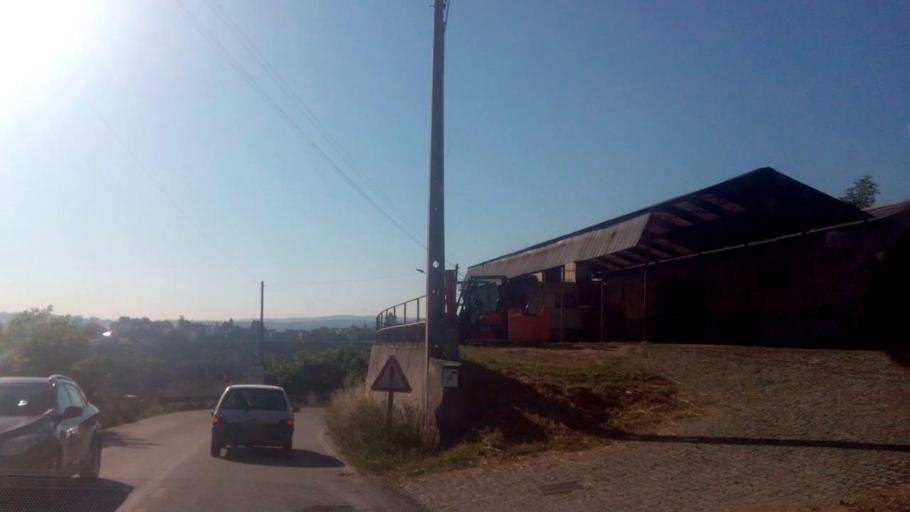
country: PT
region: Porto
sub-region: Penafiel
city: Penafiel
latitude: 41.1962
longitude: -8.2733
